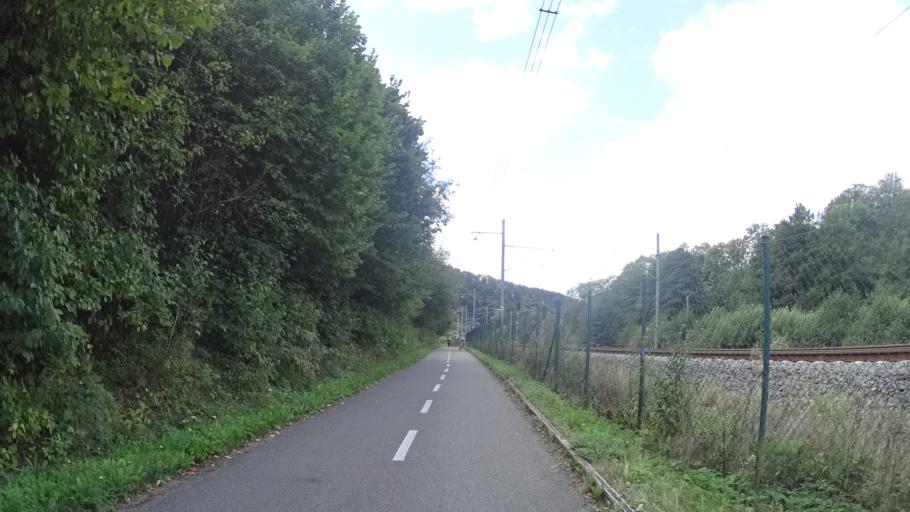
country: CZ
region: Pardubicky
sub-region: Okres Usti nad Orlici
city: Usti nad Orlici
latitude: 49.9901
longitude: 16.4439
